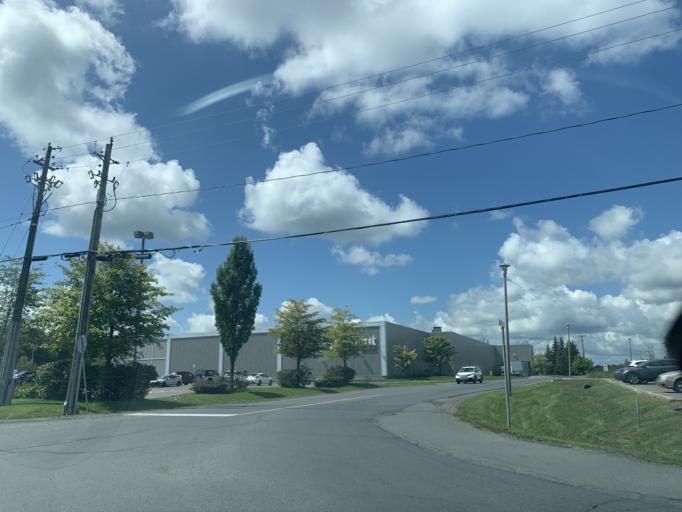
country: CA
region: Ontario
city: Hawkesbury
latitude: 45.5934
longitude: -74.6000
